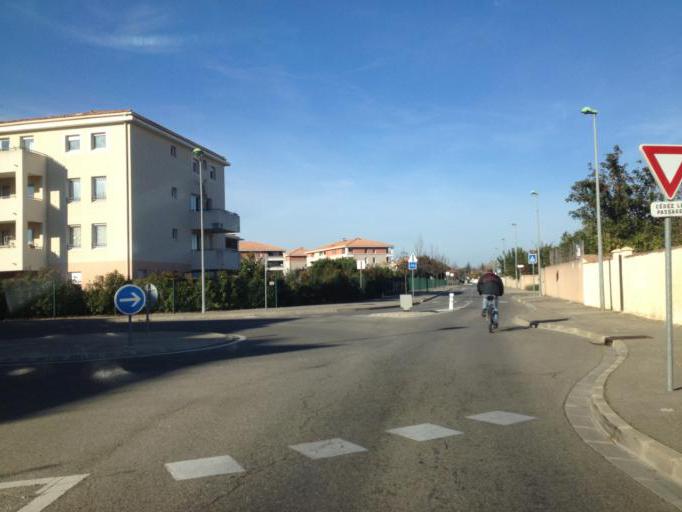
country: FR
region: Provence-Alpes-Cote d'Azur
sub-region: Departement des Bouches-du-Rhone
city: Istres
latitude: 43.5113
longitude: 4.9675
